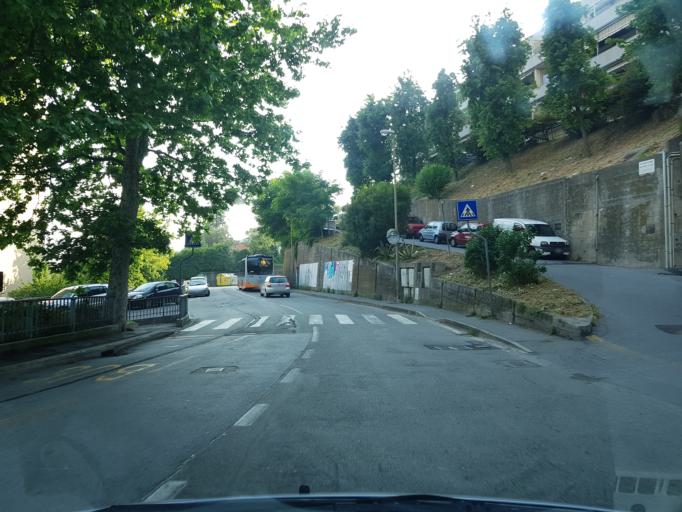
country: IT
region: Liguria
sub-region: Provincia di Genova
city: Genoa
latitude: 44.4479
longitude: 8.9072
